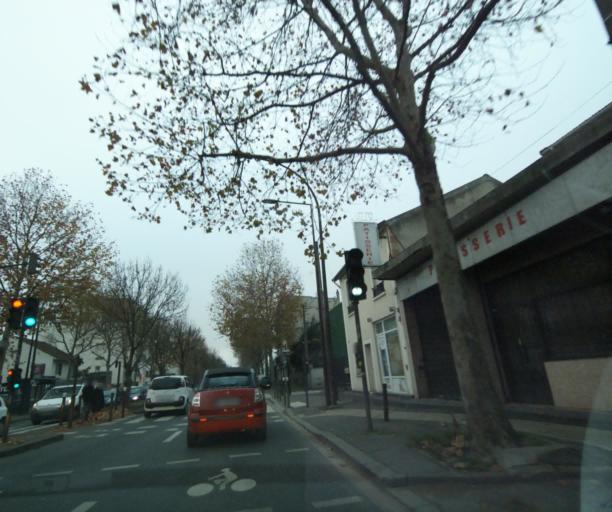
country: FR
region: Ile-de-France
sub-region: Departement de Seine-Saint-Denis
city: Livry-Gargan
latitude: 48.9150
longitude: 2.5280
